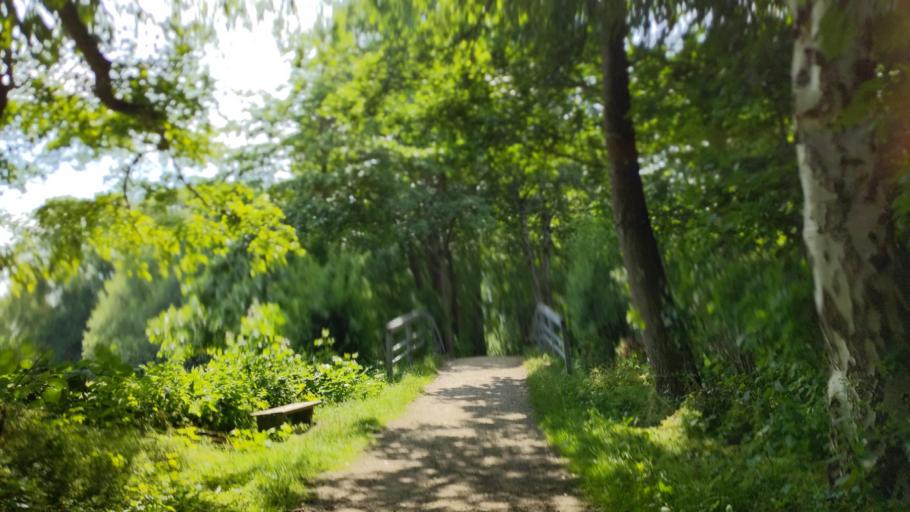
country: DE
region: Schleswig-Holstein
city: Eutin
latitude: 54.1404
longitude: 10.6372
